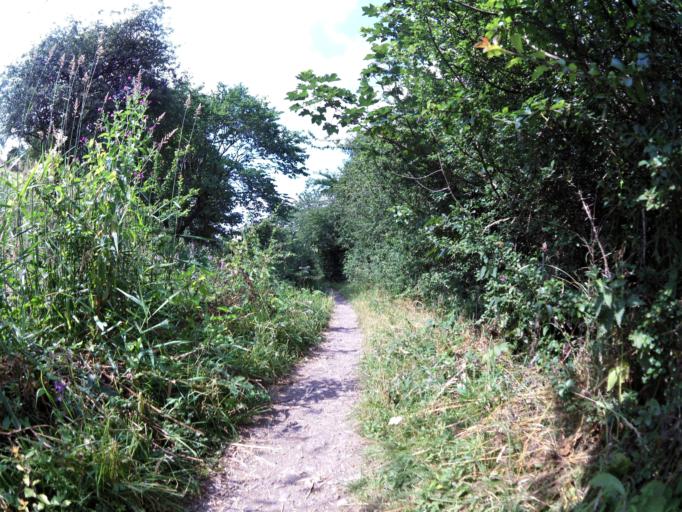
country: GB
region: Scotland
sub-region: West Lothian
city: East Calder
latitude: 55.9097
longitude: -3.4520
